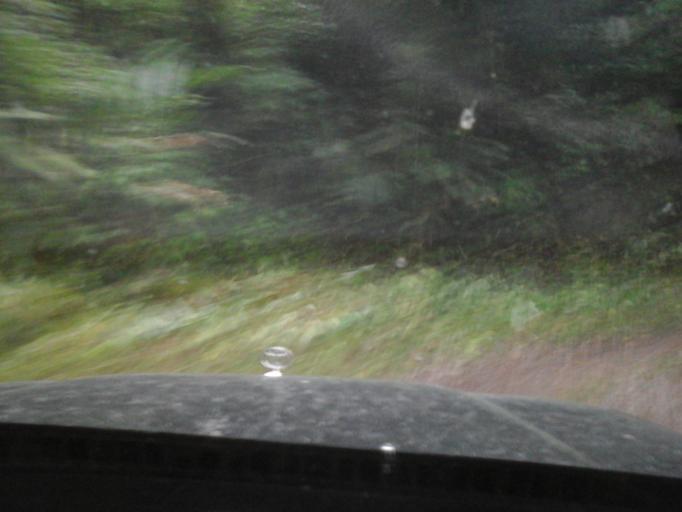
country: CO
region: Cesar
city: Agustin Codazzi
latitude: 9.9404
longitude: -73.1228
